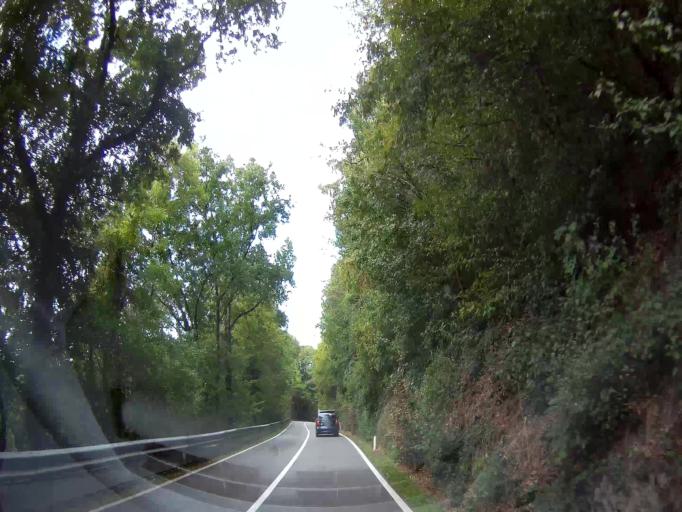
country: BE
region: Wallonia
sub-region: Province de Liege
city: Hamoir
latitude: 50.3900
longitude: 5.5396
